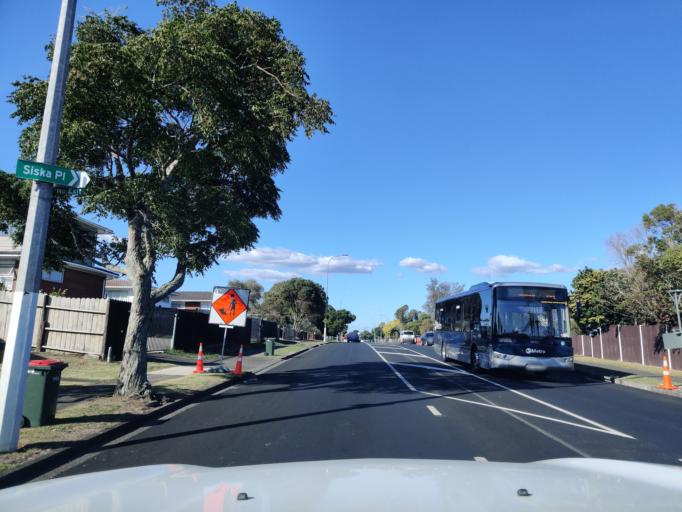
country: NZ
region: Auckland
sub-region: Auckland
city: Takanini
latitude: -37.0385
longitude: 174.8867
